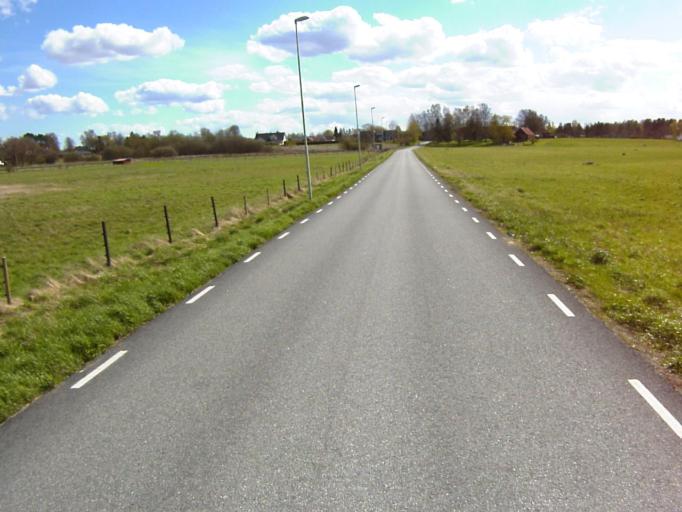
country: SE
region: Skane
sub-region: Kristianstads Kommun
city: Kristianstad
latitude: 56.0147
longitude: 14.0906
